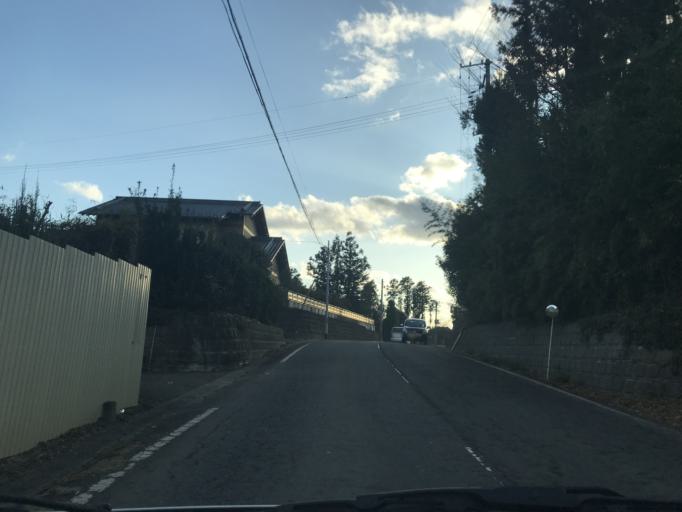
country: JP
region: Miyagi
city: Kogota
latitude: 38.6357
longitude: 141.0685
